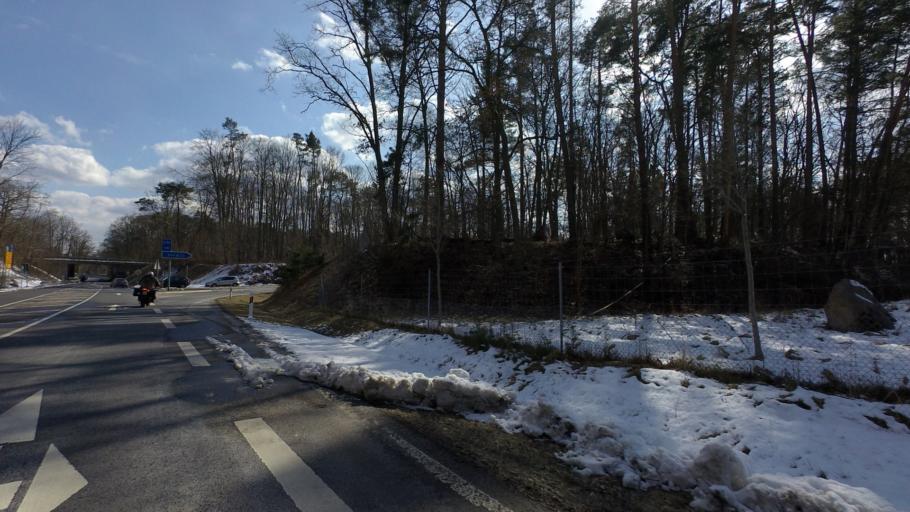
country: DE
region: Brandenburg
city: Joachimsthal
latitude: 52.8935
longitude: 13.7176
